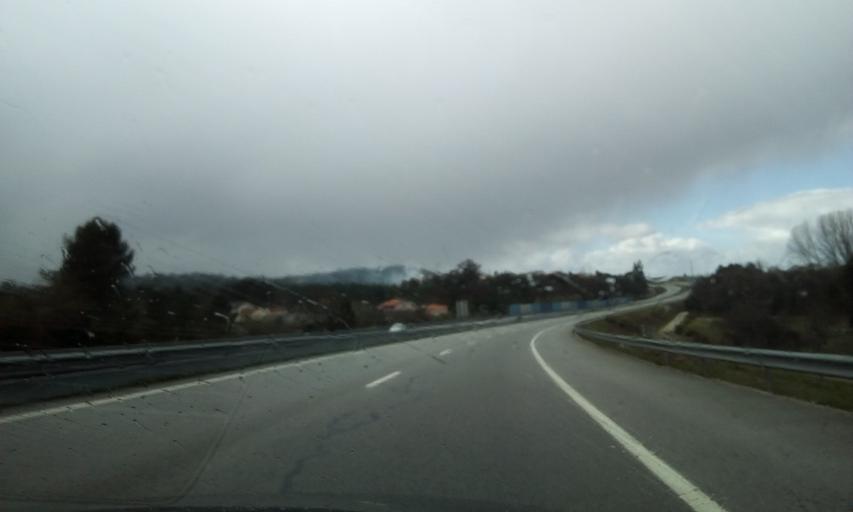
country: PT
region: Viseu
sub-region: Mangualde
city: Mangualde
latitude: 40.6128
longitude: -7.7116
